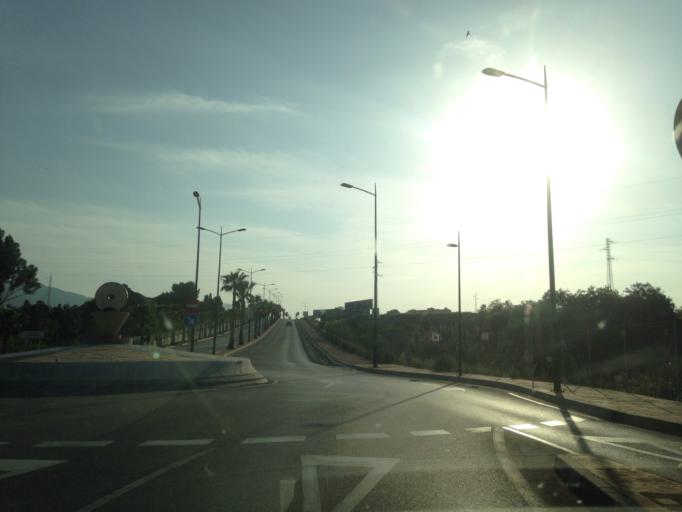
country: ES
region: Andalusia
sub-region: Provincia de Malaga
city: Alhaurin de la Torre
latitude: 36.6698
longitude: -4.5571
